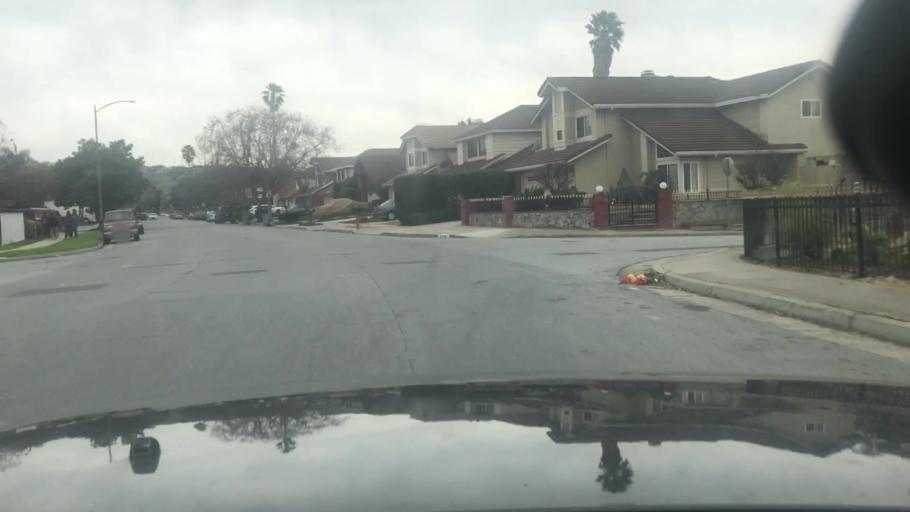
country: US
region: California
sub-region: Santa Clara County
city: Seven Trees
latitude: 37.3108
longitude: -121.8048
